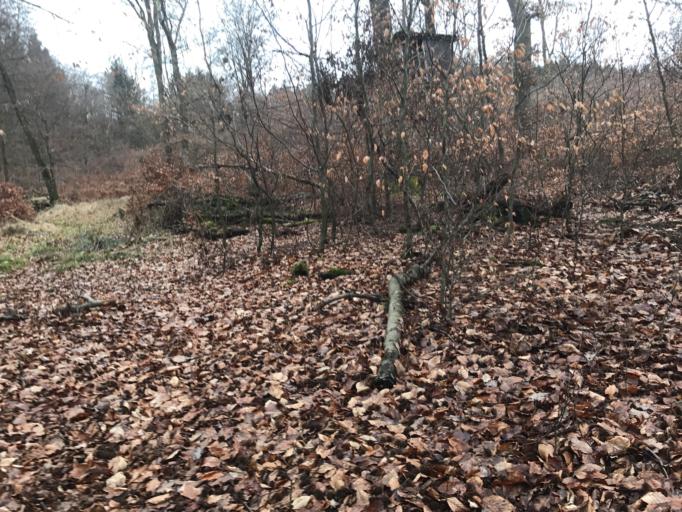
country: DE
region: Hesse
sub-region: Regierungsbezirk Darmstadt
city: Niedernhausen
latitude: 50.1508
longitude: 8.2924
